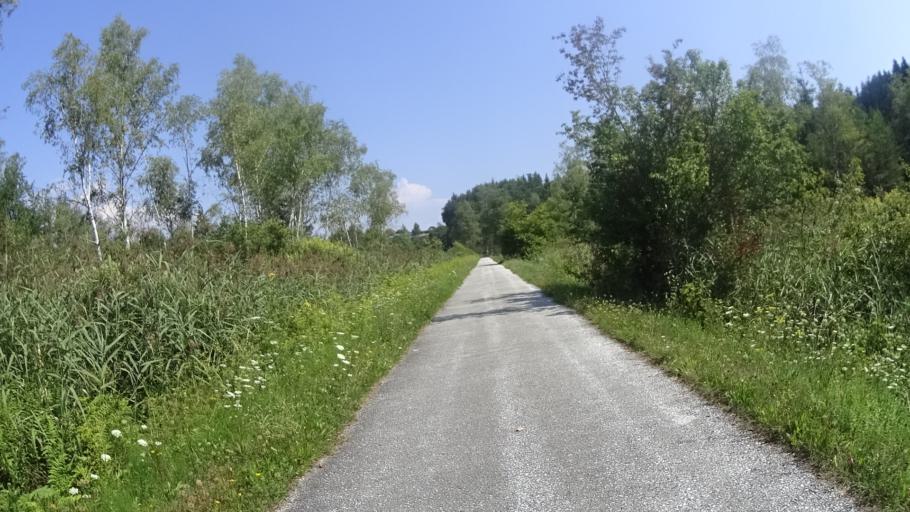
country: AT
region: Carinthia
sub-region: Politischer Bezirk Volkermarkt
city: Eberndorf
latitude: 46.5667
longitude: 14.6297
